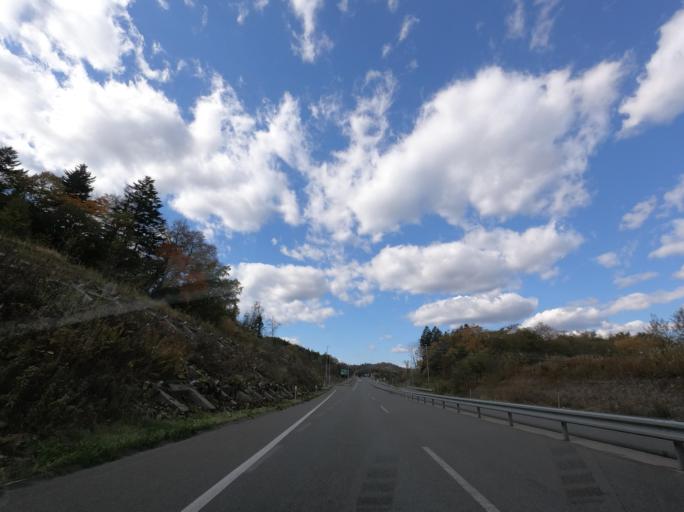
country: JP
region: Hokkaido
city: Kushiro
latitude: 43.0763
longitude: 144.0674
